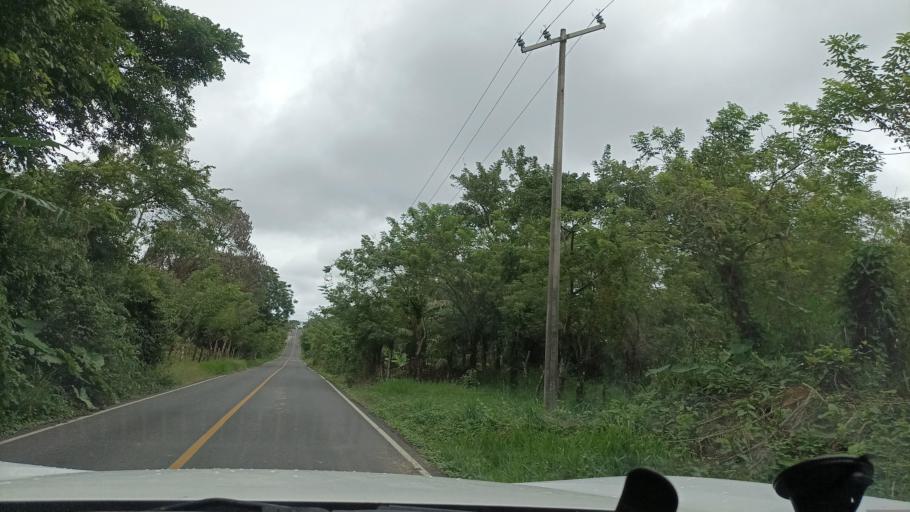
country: MX
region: Veracruz
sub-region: Moloacan
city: Cuichapa
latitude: 17.8052
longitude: -94.3566
